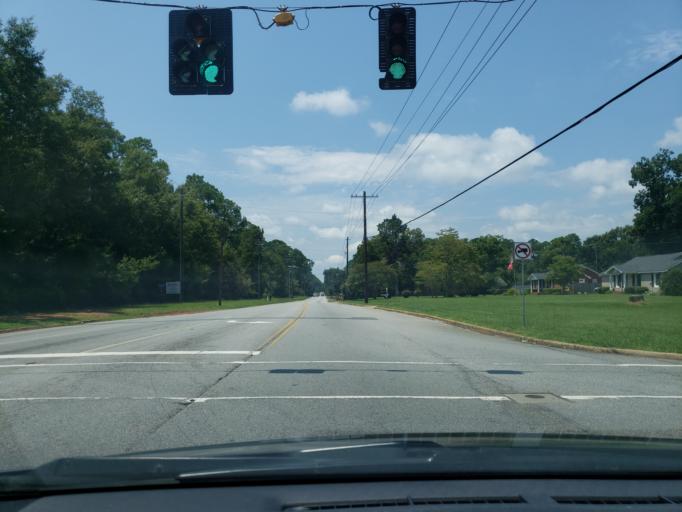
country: US
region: Georgia
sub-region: Dougherty County
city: Albany
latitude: 31.6135
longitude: -84.2255
